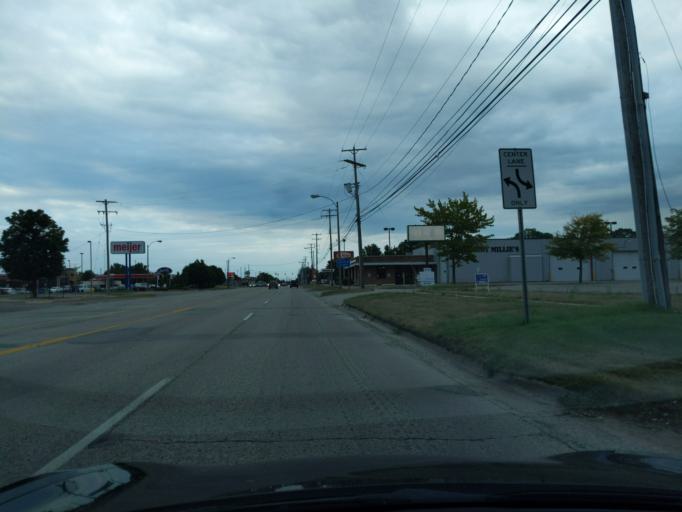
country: US
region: Michigan
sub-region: Isabella County
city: Mount Pleasant
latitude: 43.6117
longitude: -84.7664
